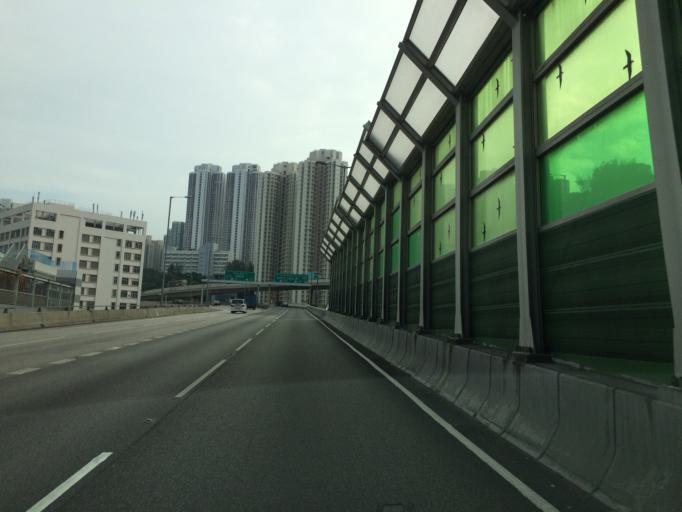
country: HK
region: Kowloon City
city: Kowloon
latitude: 22.3087
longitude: 114.2283
